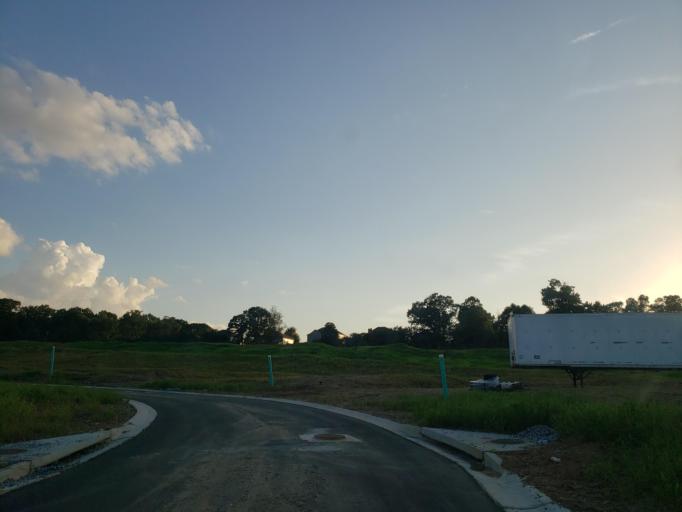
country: US
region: Georgia
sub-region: Forsyth County
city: Cumming
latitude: 34.2198
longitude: -84.2165
